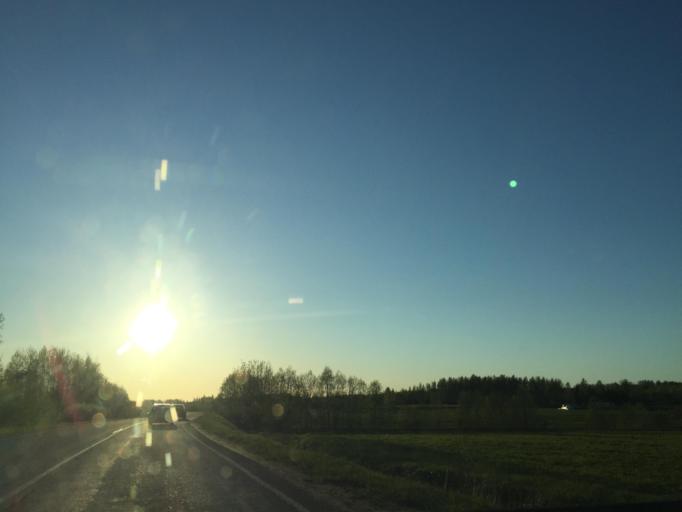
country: LV
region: Skriveri
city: Skriveri
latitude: 56.8831
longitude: 25.2408
